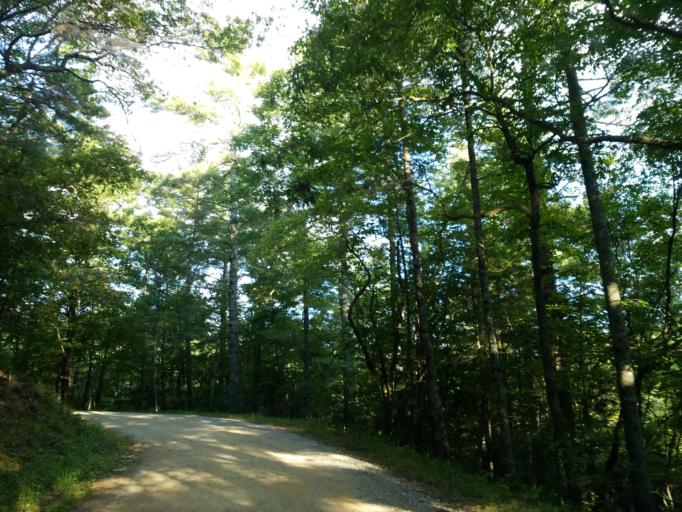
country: US
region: Georgia
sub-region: Union County
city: Blairsville
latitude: 34.7488
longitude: -84.0698
